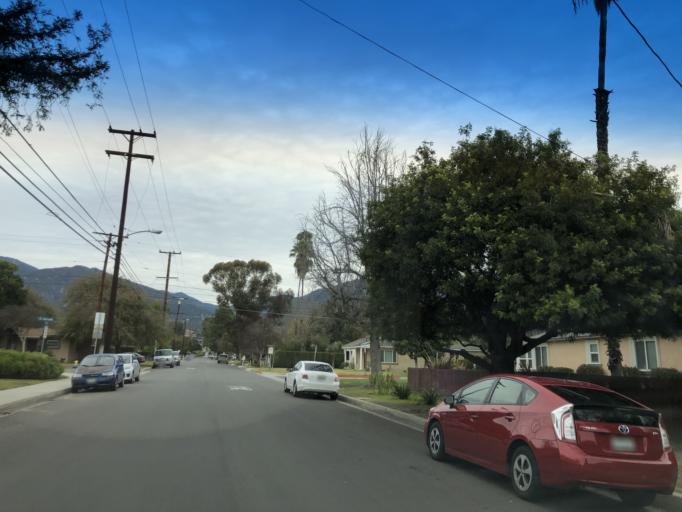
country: US
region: California
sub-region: Los Angeles County
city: Arcadia
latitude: 34.1343
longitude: -118.0203
